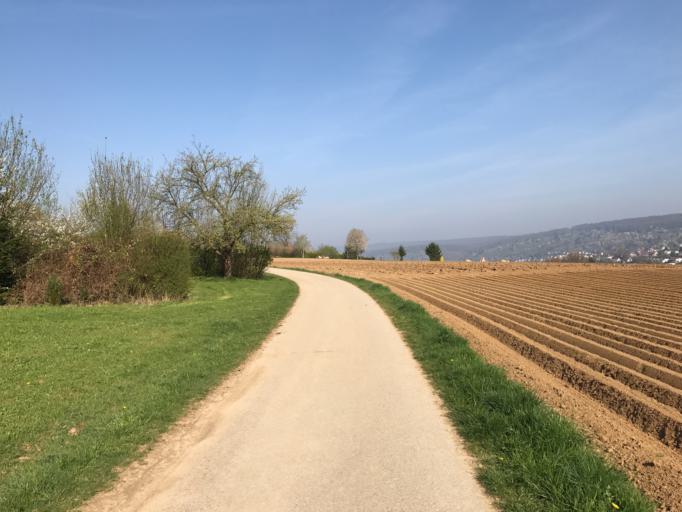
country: DE
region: Baden-Wuerttemberg
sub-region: Regierungsbezirk Stuttgart
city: Wernau
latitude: 48.6973
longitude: 9.4293
